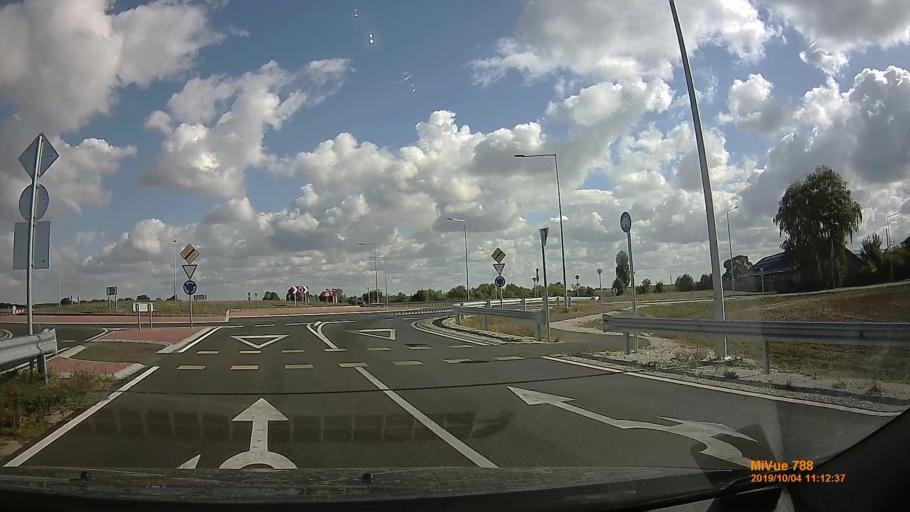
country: HU
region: Somogy
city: Kaposvar
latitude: 46.4246
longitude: 17.7741
